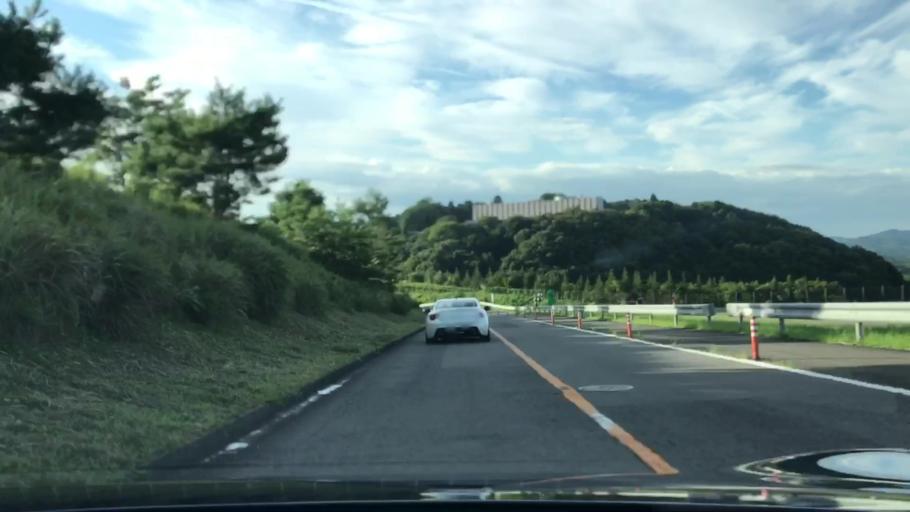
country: JP
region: Tochigi
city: Motegi
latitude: 36.5348
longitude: 140.2309
